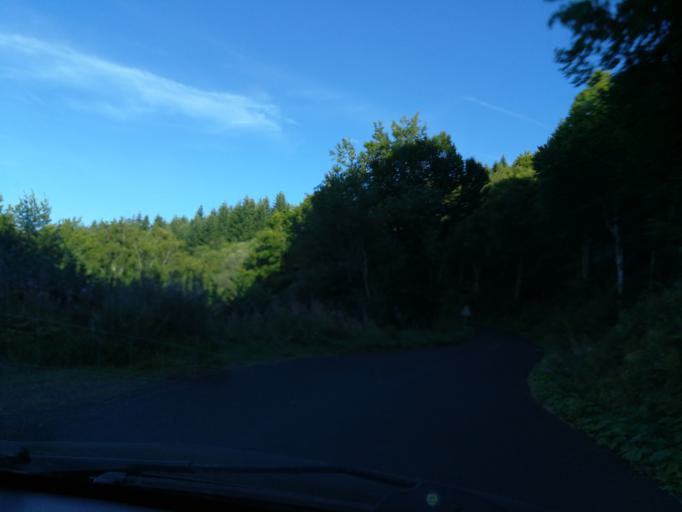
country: FR
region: Auvergne
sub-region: Departement du Cantal
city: Vic-sur-Cere
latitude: 45.0778
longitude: 2.5616
